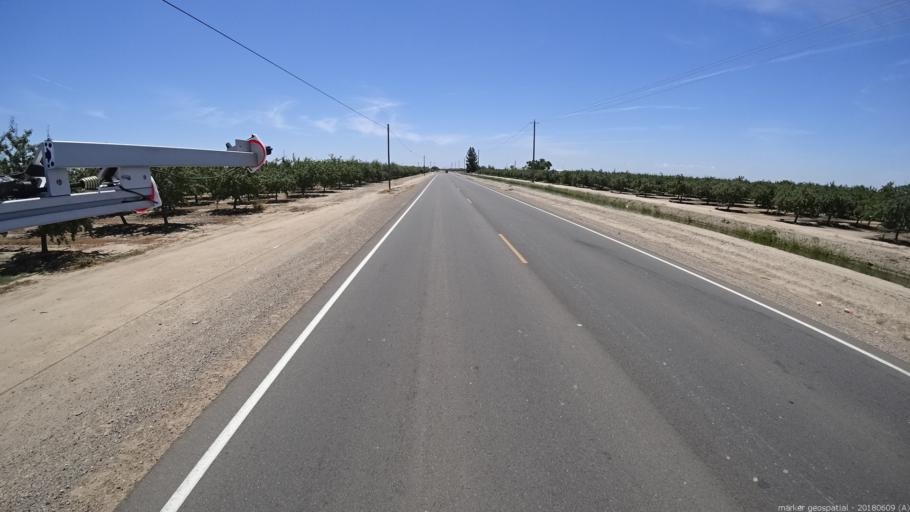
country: US
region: California
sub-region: Madera County
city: Parkwood
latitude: 36.9297
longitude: -120.0741
